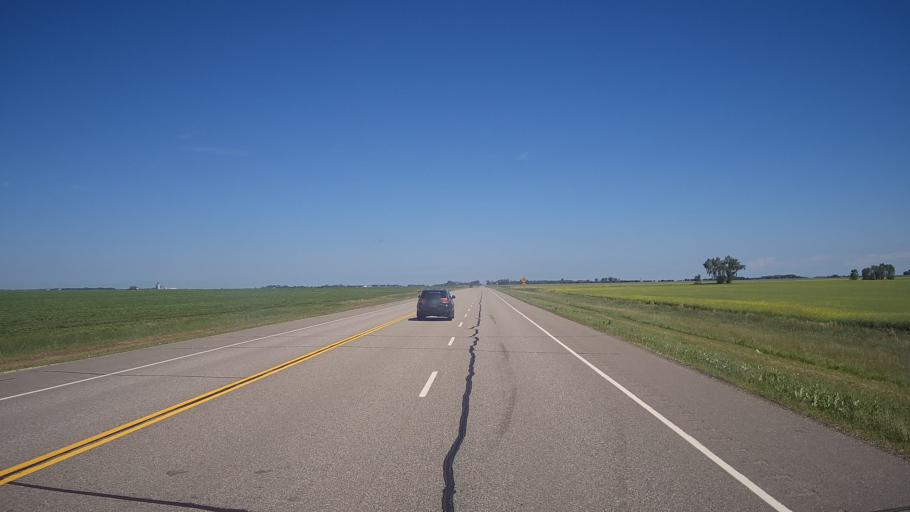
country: CA
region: Manitoba
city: Portage la Prairie
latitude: 50.0268
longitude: -98.4687
